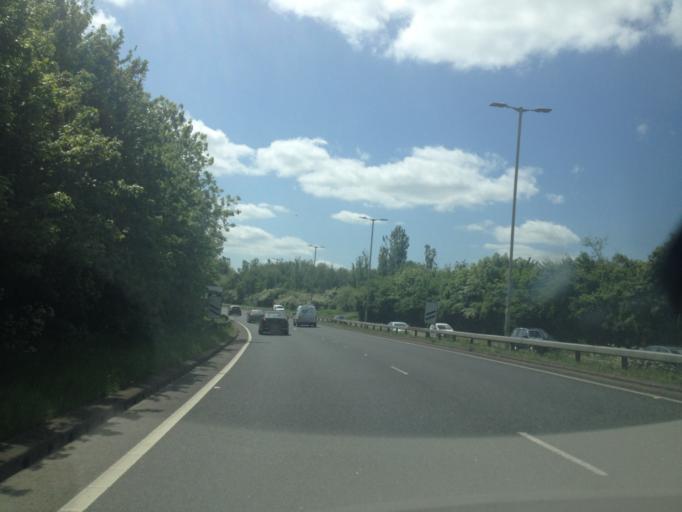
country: GB
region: England
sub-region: Hertfordshire
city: Watford
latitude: 51.6688
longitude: -0.3812
